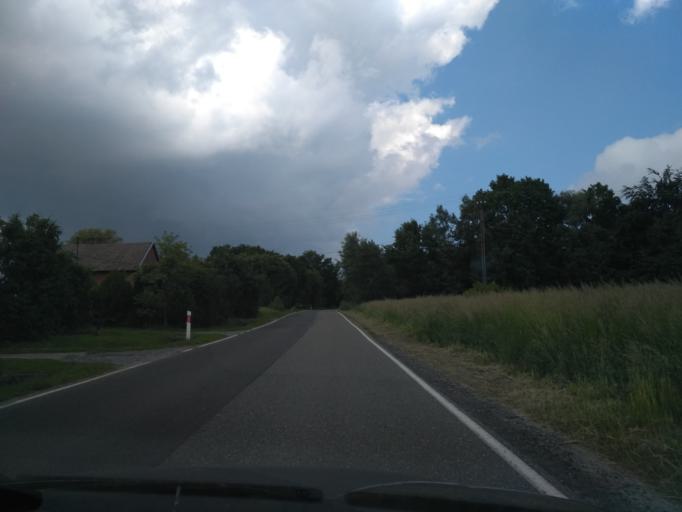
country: PL
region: Subcarpathian Voivodeship
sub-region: Powiat lancucki
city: Handzlowka
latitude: 49.9622
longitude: 22.1950
